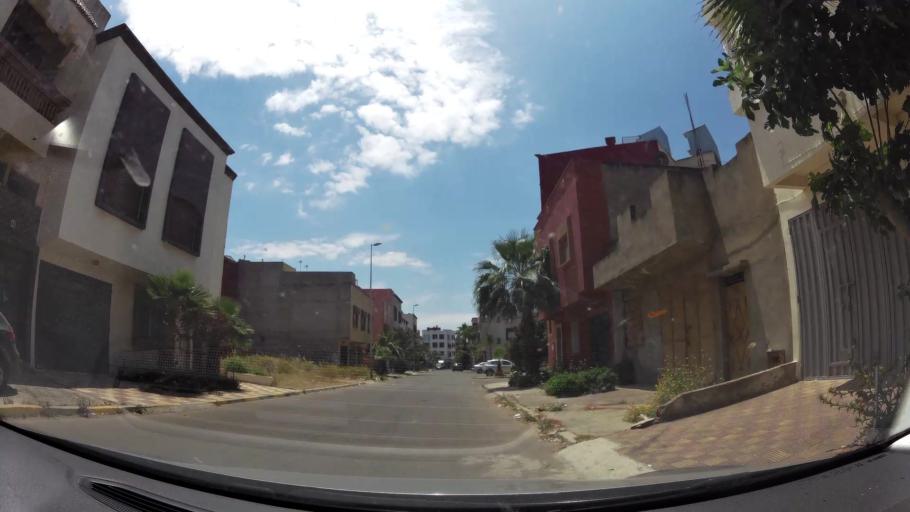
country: MA
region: Gharb-Chrarda-Beni Hssen
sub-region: Kenitra Province
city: Kenitra
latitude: 34.2697
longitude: -6.6170
